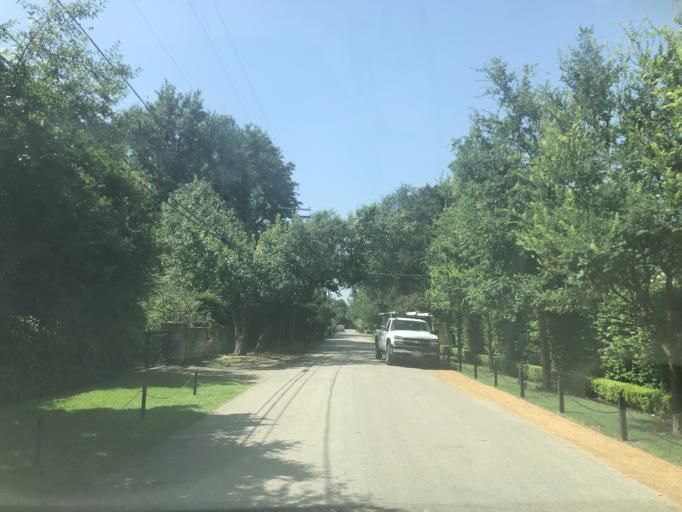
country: US
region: Texas
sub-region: Dallas County
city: University Park
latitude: 32.8737
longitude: -96.8175
